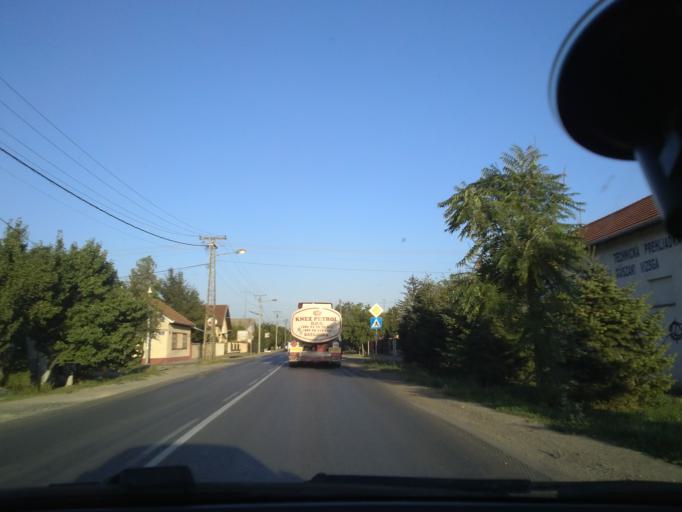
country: RS
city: Rumenka
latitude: 45.2912
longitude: 19.7457
